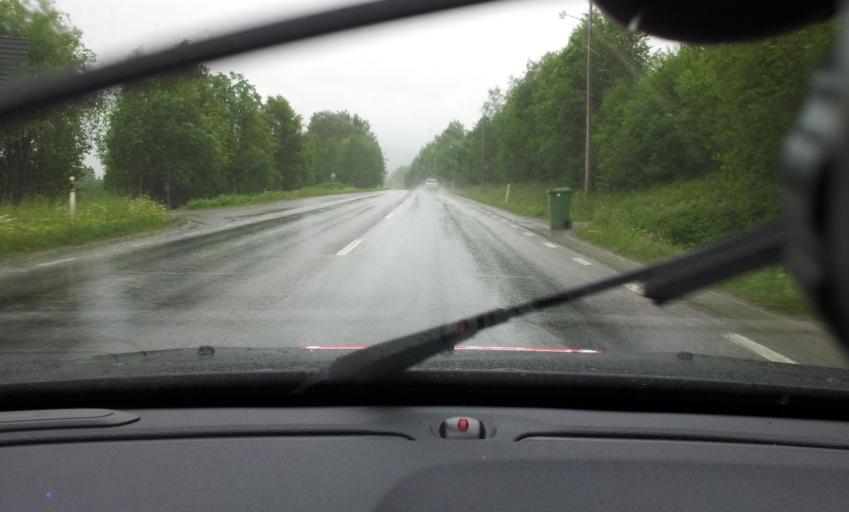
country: SE
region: Jaemtland
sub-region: Are Kommun
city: Are
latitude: 63.3577
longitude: 13.1822
